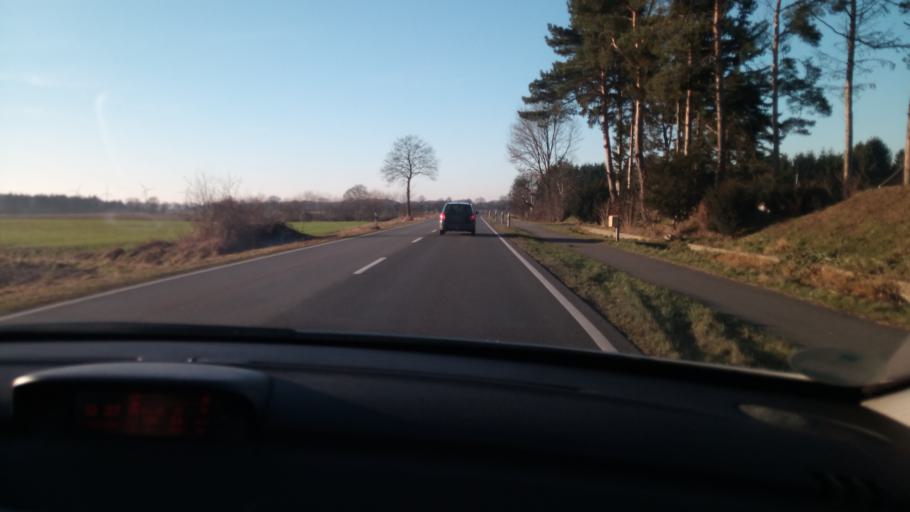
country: DE
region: Schleswig-Holstein
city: Lauenburg
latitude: 53.3646
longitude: 10.5365
